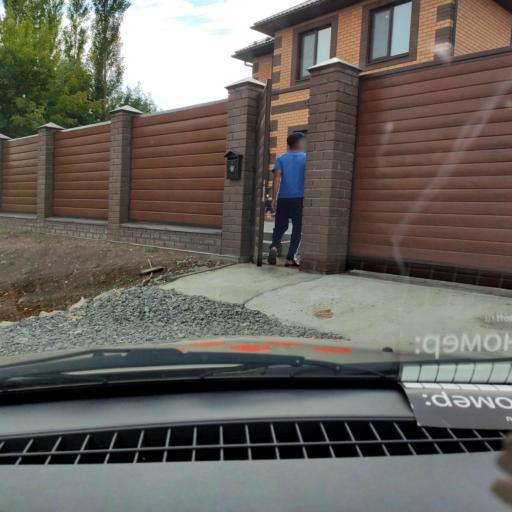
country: RU
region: Bashkortostan
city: Ufa
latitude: 54.6188
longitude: 55.9210
